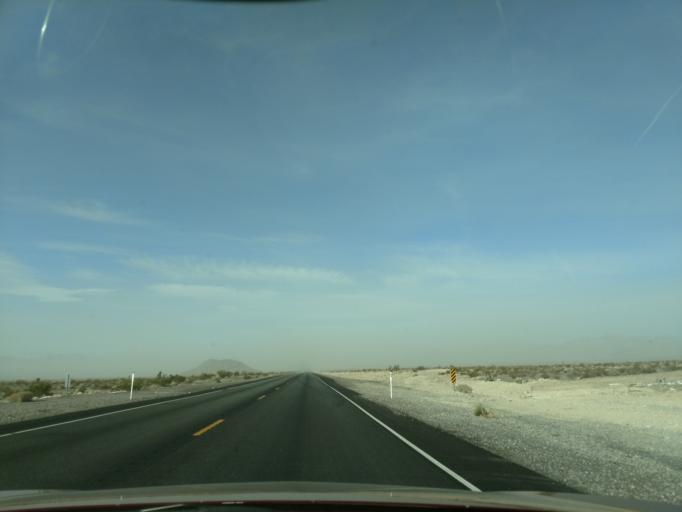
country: US
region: Nevada
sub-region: Nye County
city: Pahrump
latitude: 36.5663
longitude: -116.1332
